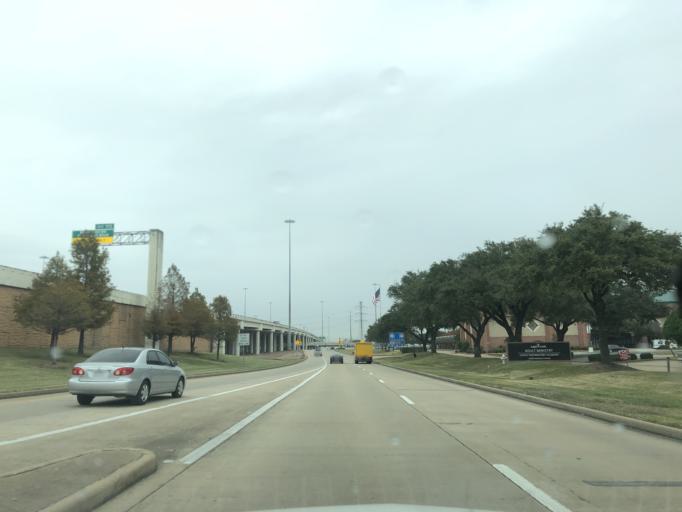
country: US
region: Texas
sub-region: Fort Bend County
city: Meadows Place
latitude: 29.6251
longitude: -95.5958
